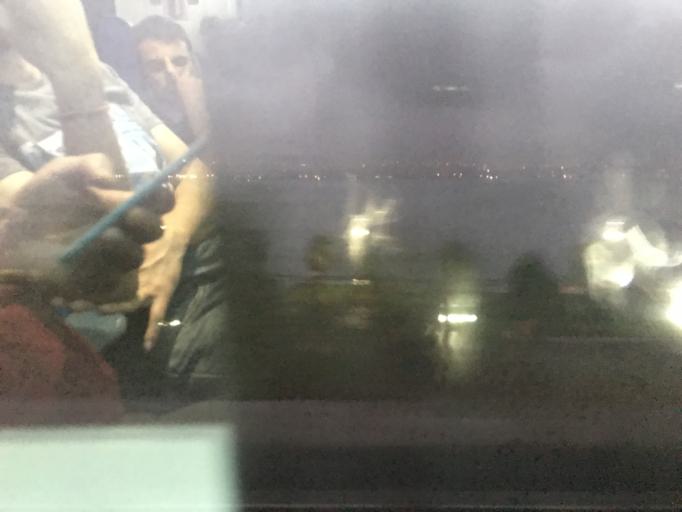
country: TR
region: Kocaeli
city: Derince
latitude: 40.7492
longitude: 29.8048
